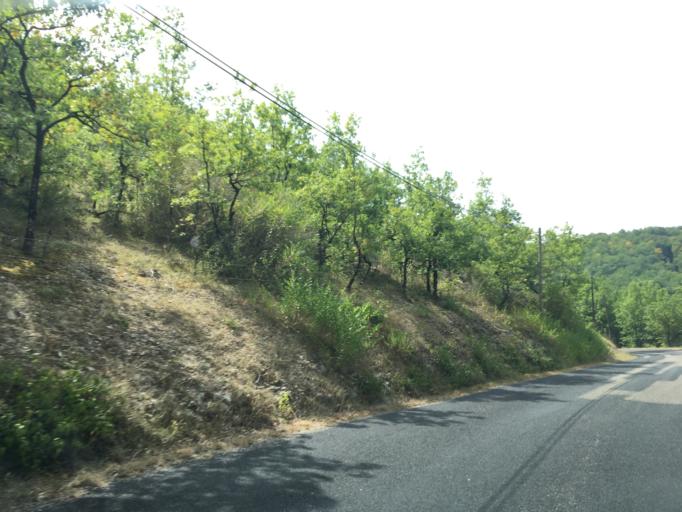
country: FR
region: Midi-Pyrenees
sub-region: Departement du Lot
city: Le Vigan
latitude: 44.7462
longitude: 1.5089
